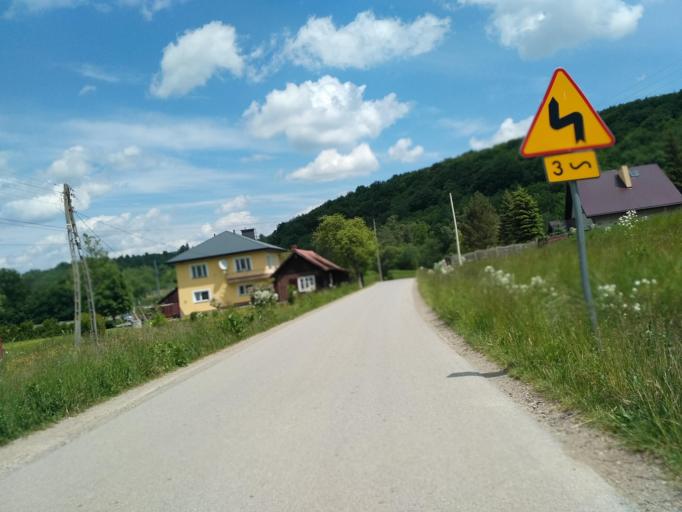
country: PL
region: Subcarpathian Voivodeship
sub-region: Powiat krosnienski
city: Dukla
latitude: 49.5787
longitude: 21.6222
